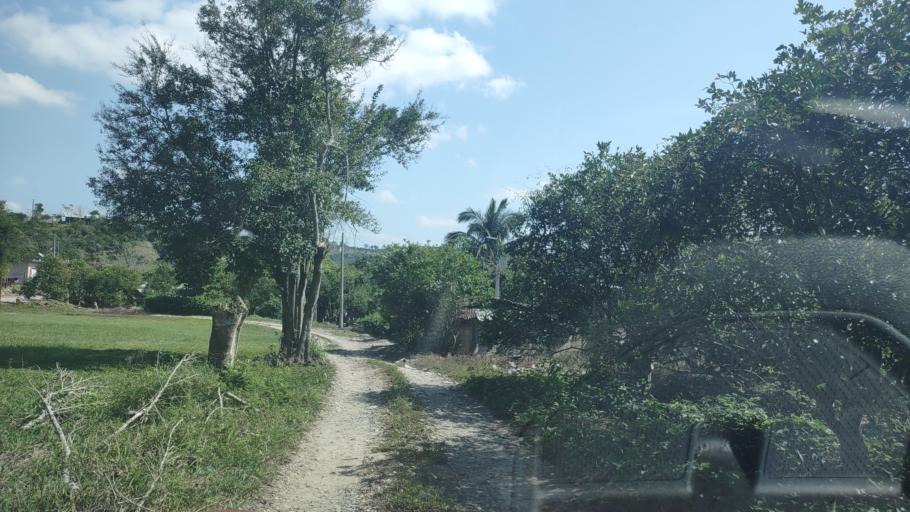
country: MX
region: Veracruz
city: Agua Dulce
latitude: 20.2917
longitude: -97.1528
